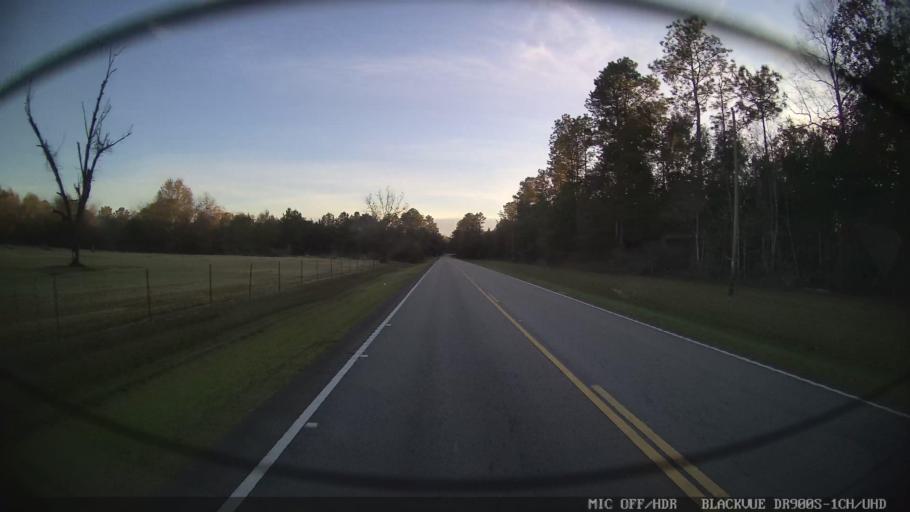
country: US
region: Mississippi
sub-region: Stone County
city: Wiggins
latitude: 31.0081
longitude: -89.2570
